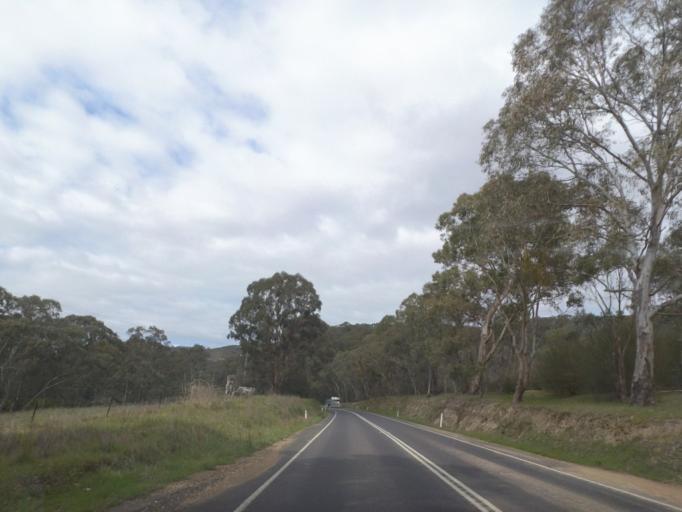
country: AU
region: Victoria
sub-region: Murrindindi
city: Kinglake West
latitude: -37.1366
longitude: 145.2319
